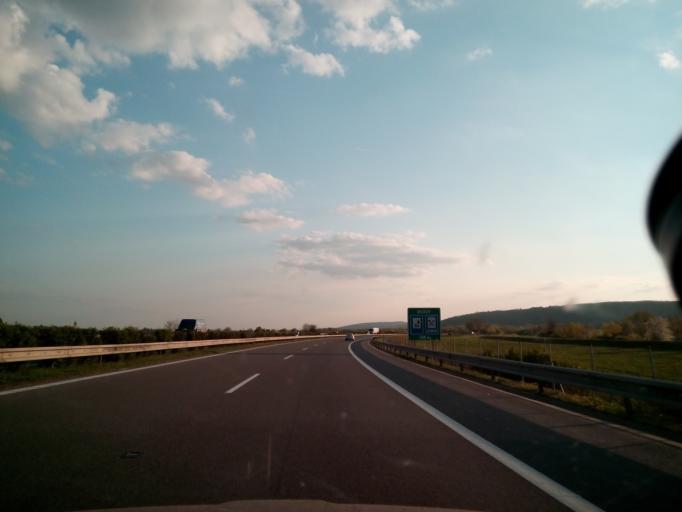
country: SK
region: Trenciansky
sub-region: Okres Nove Mesto nad Vahom
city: Nove Mesto nad Vahom
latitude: 48.8042
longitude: 17.9028
